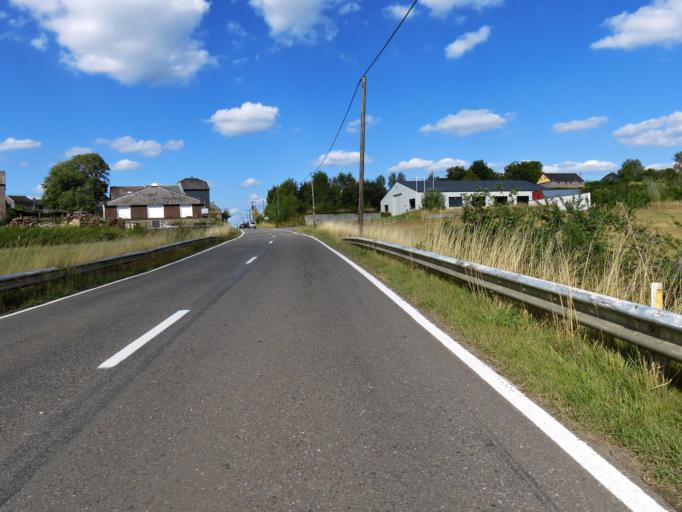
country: BE
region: Wallonia
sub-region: Province de Namur
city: Bievre
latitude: 49.8904
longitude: 5.0057
